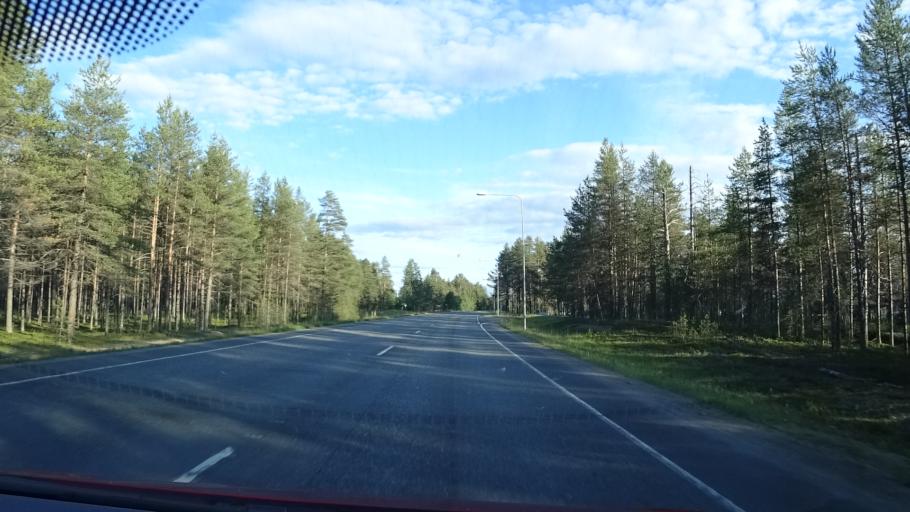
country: FI
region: Northern Ostrobothnia
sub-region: Koillismaa
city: Kuusamo
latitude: 66.0073
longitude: 29.1524
